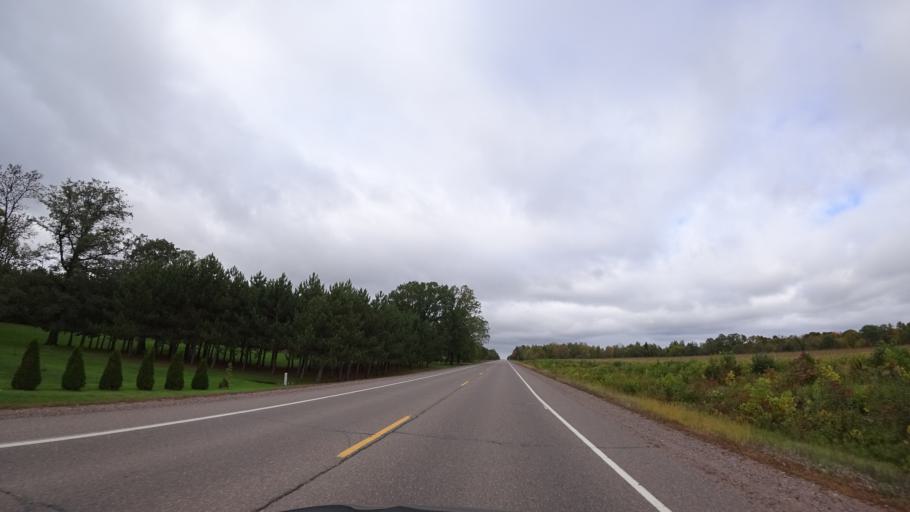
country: US
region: Wisconsin
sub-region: Rusk County
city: Ladysmith
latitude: 45.5094
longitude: -91.1115
